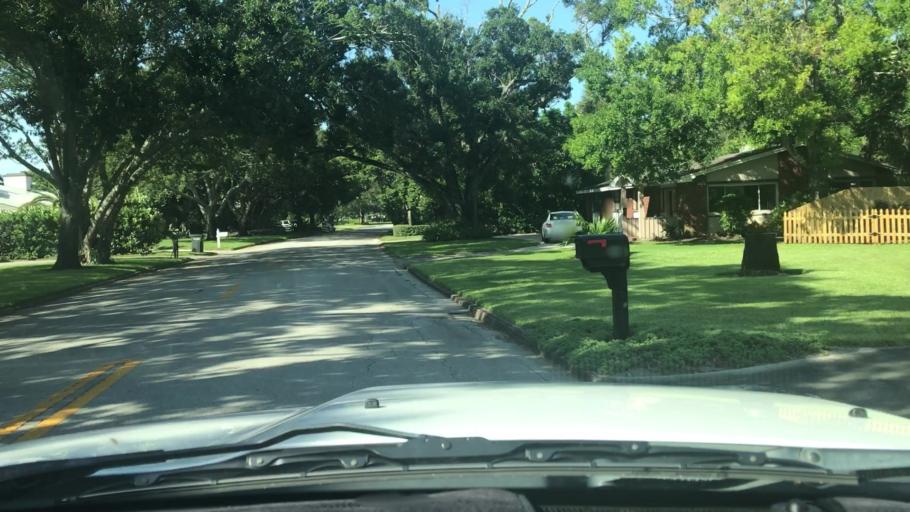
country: US
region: Florida
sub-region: Indian River County
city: Vero Beach
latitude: 27.6399
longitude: -80.4106
